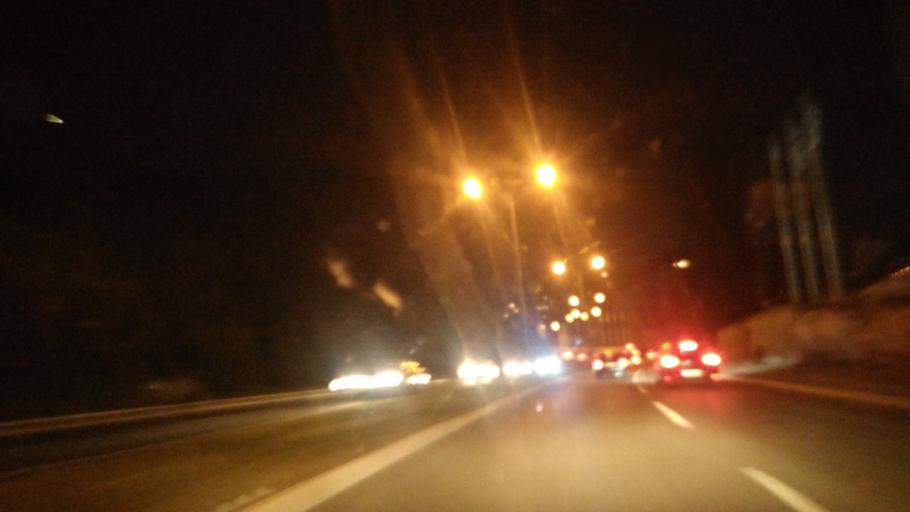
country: RS
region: Central Serbia
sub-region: Belgrade
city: Cukarica
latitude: 44.7682
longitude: 20.4118
